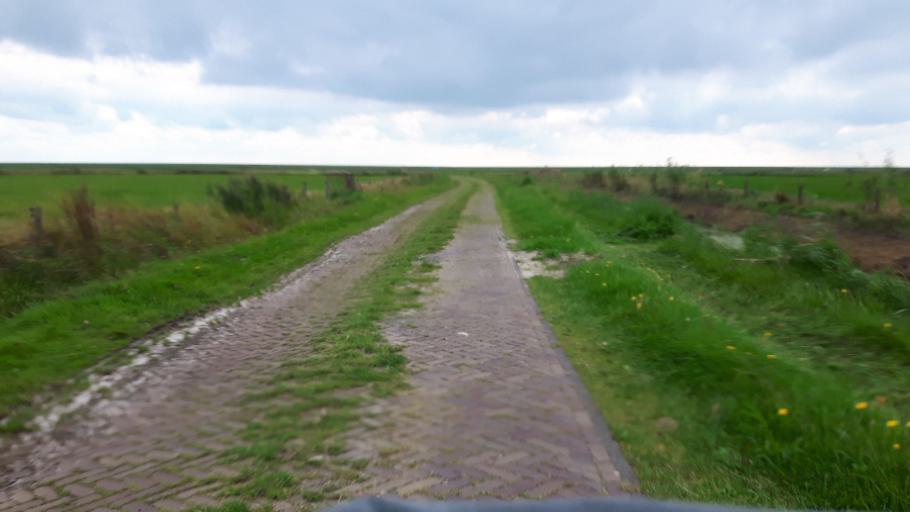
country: NL
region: Friesland
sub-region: Gemeente Ameland
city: Nes
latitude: 53.4476
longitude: 5.8195
